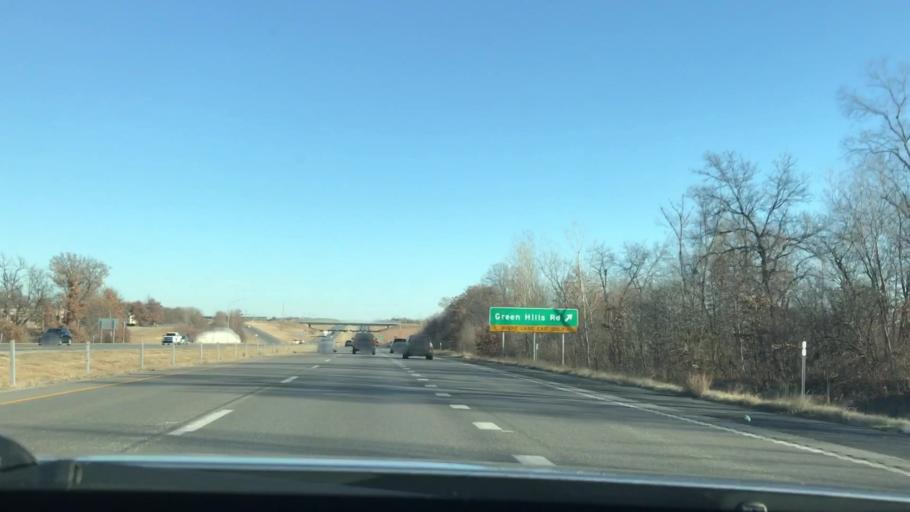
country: US
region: Missouri
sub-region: Platte County
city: Weatherby Lake
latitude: 39.2542
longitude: -94.6403
